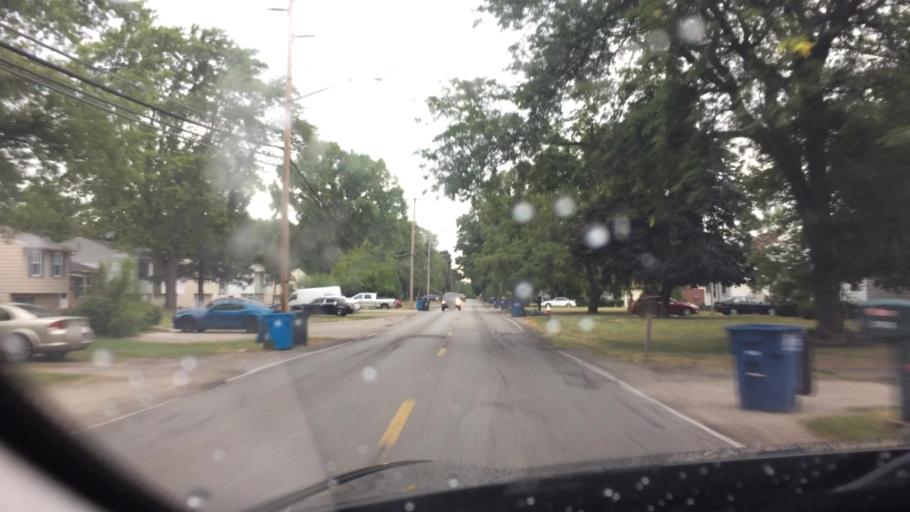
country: US
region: Ohio
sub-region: Lucas County
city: Ottawa Hills
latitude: 41.6423
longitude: -83.6406
